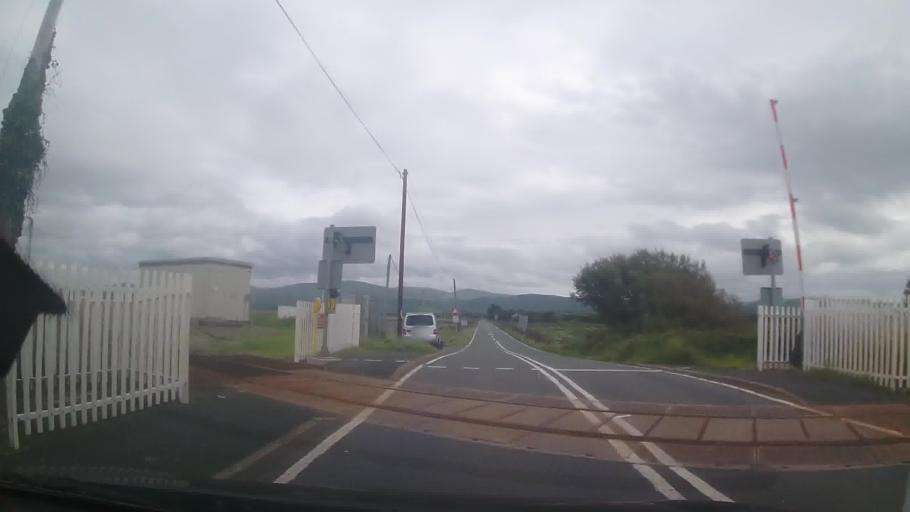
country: GB
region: Wales
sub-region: County of Ceredigion
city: Bow Street
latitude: 52.5186
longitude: -4.0387
